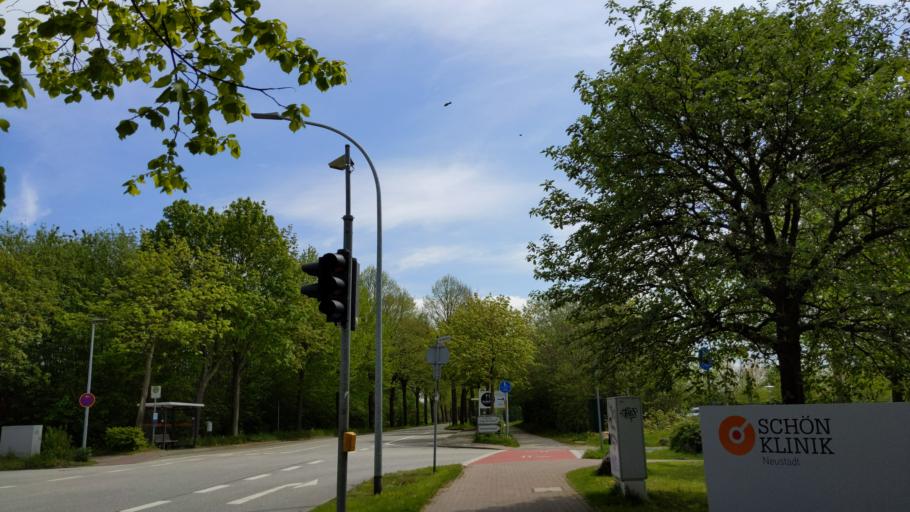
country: DE
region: Schleswig-Holstein
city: Neustadt in Holstein
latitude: 54.0927
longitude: 10.8288
